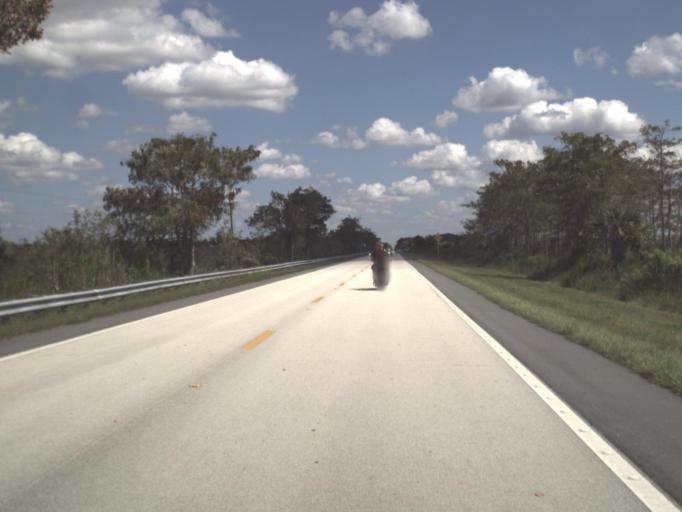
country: US
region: Florida
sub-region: Collier County
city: Marco
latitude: 25.8743
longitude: -81.2046
